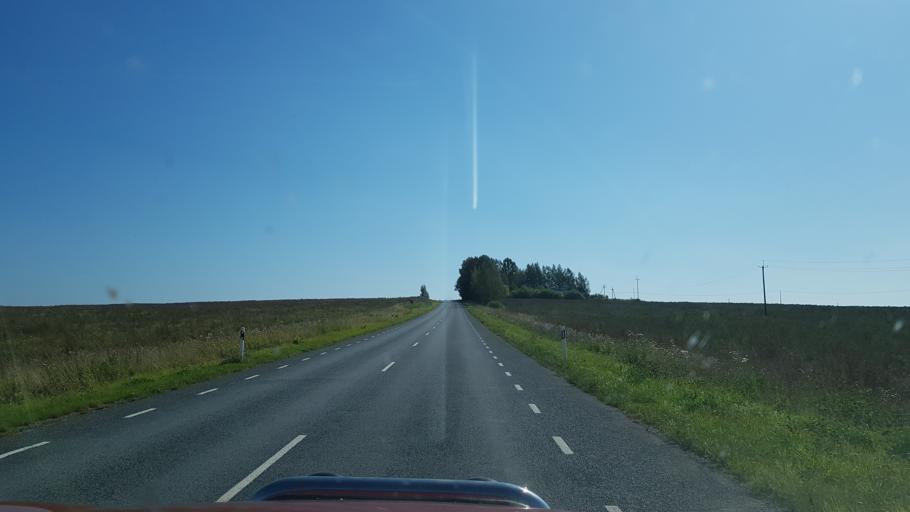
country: EE
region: Polvamaa
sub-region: Polva linn
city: Polva
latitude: 58.2791
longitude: 27.0629
